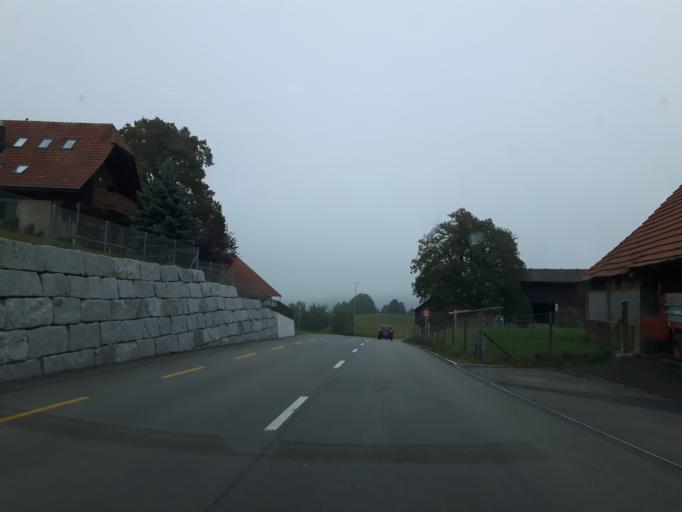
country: CH
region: Lucerne
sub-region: Willisau District
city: Pfaffnau
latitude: 47.2213
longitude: 7.8852
